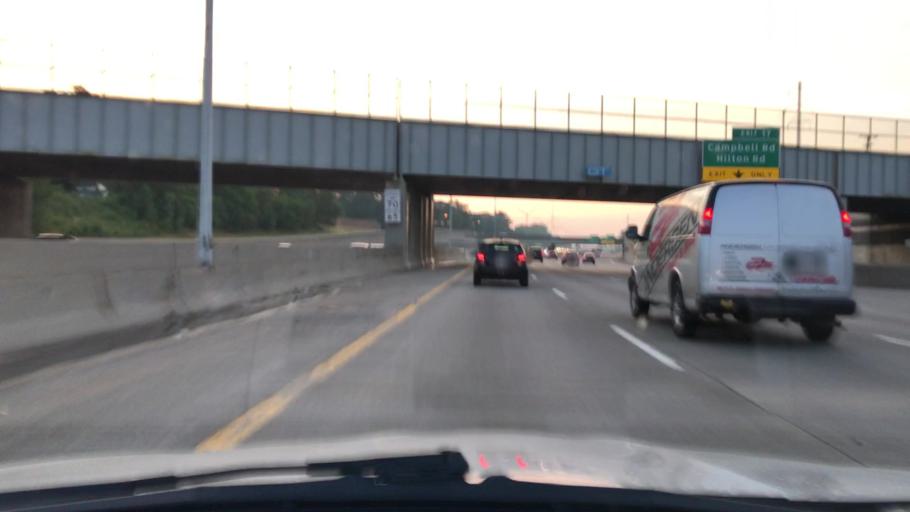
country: US
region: Michigan
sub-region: Oakland County
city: Pleasant Ridge
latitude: 42.4755
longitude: -83.1369
